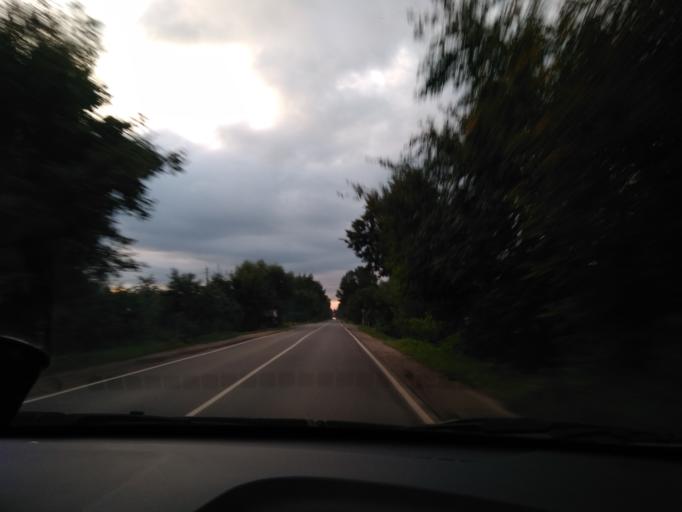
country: RU
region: Moskovskaya
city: Ramenskoye
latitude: 55.5038
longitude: 38.1871
